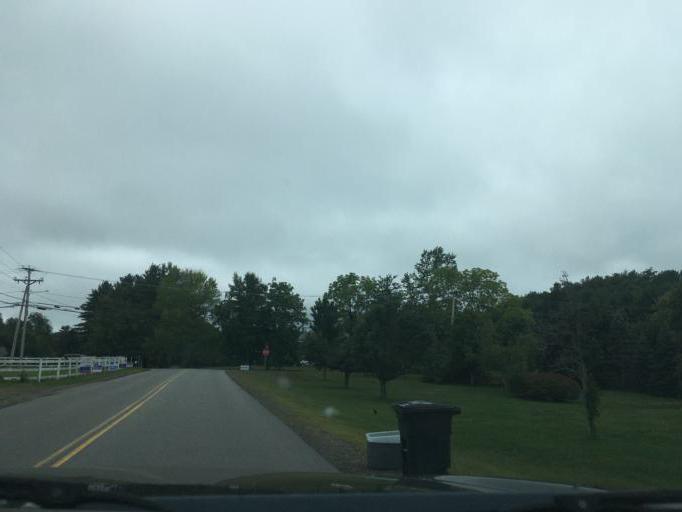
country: US
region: New Hampshire
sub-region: Rockingham County
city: Stratham Station
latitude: 42.9985
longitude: -70.8861
